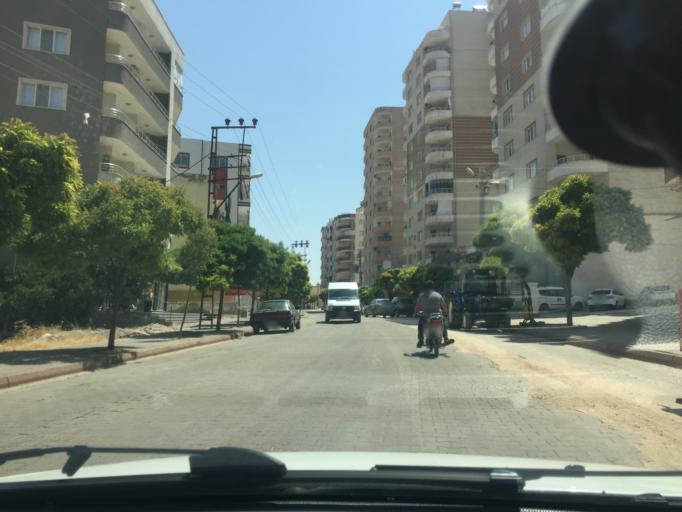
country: TR
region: Mardin
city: Midyat
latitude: 37.4309
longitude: 41.3369
